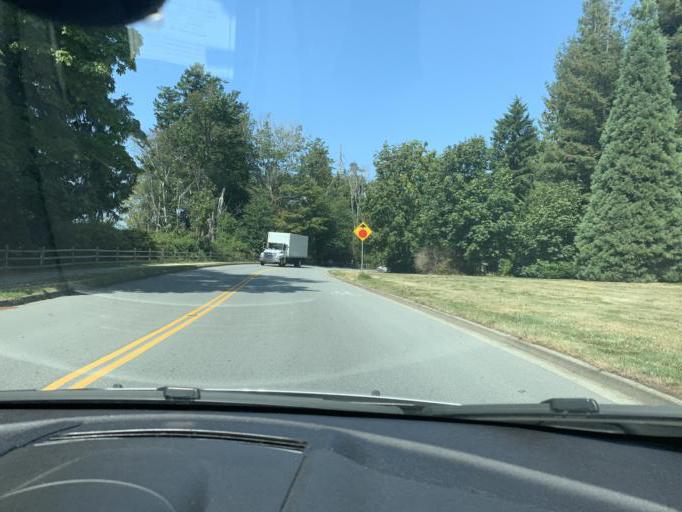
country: CA
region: British Columbia
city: West End
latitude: 49.2615
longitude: -123.2579
